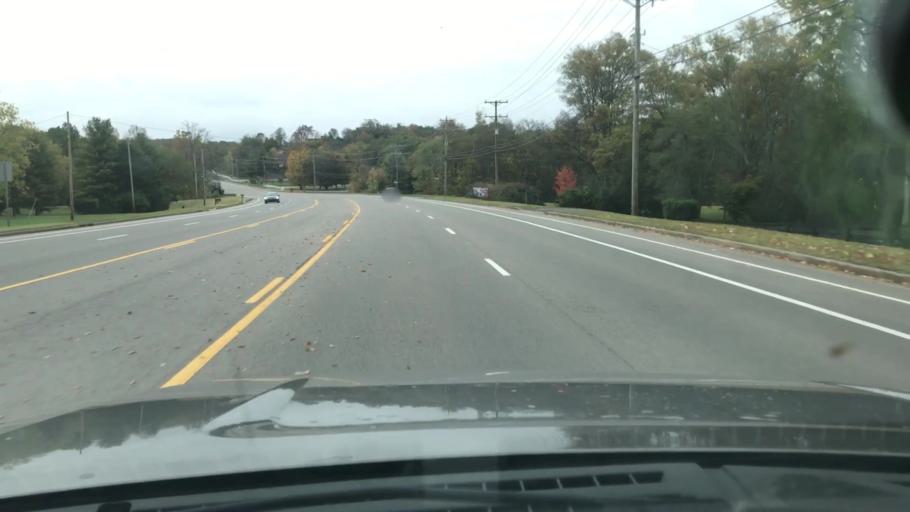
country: US
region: Tennessee
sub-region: Williamson County
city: Franklin
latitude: 35.9767
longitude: -86.8877
